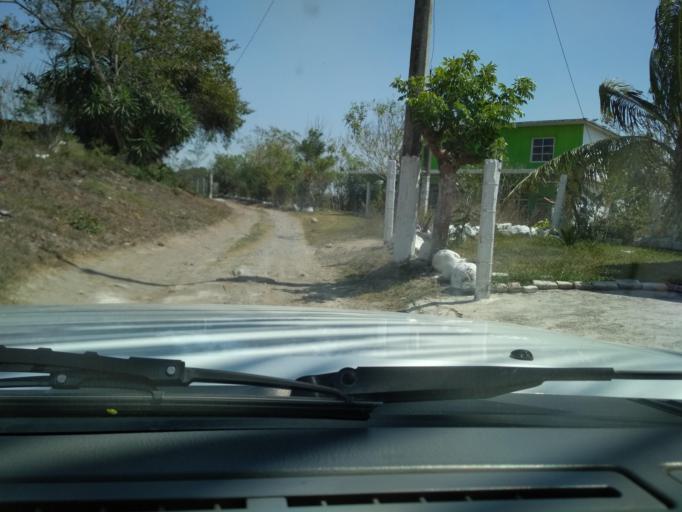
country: MX
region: Veracruz
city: Manlio Fabio Altamirano
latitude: 19.1546
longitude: -96.3285
